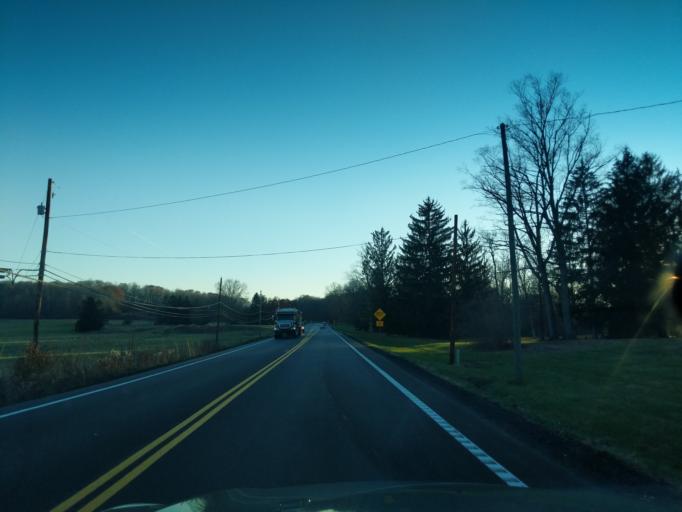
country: US
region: Ohio
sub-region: Licking County
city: Harbor Hills
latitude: 39.9825
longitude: -82.4093
